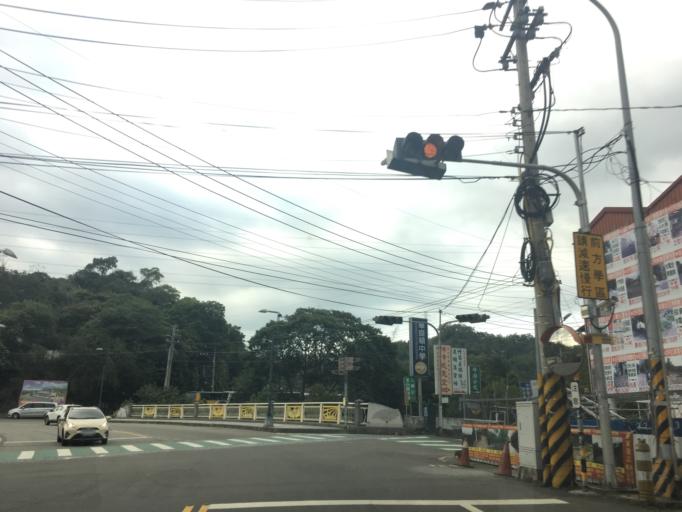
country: TW
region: Taiwan
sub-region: Taichung City
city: Taichung
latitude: 24.1587
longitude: 120.7443
